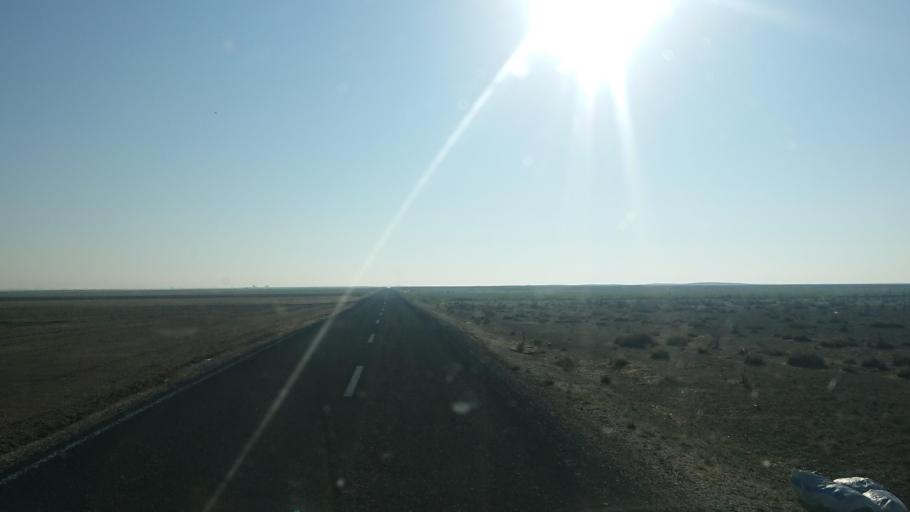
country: TR
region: Aksaray
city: Yesilova
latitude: 38.3879
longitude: 33.7603
